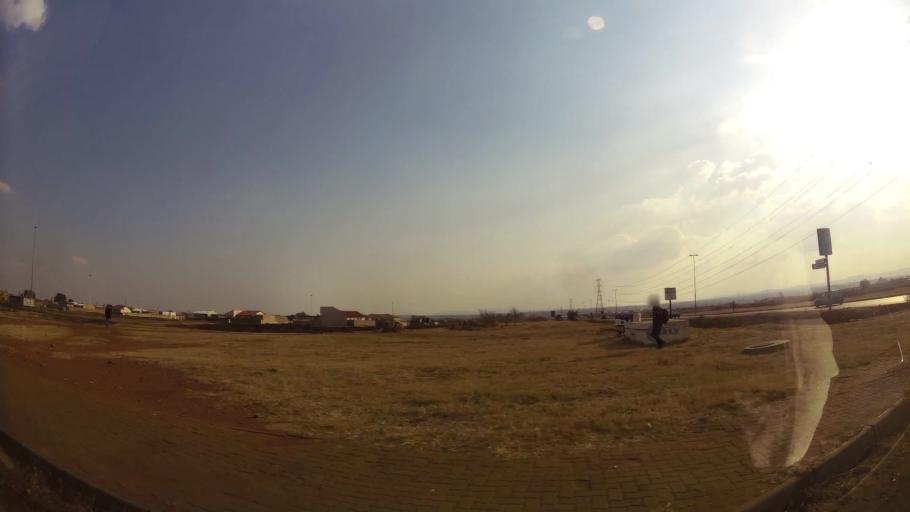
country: ZA
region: Gauteng
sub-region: Ekurhuleni Metropolitan Municipality
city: Germiston
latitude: -26.3438
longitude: 28.1956
